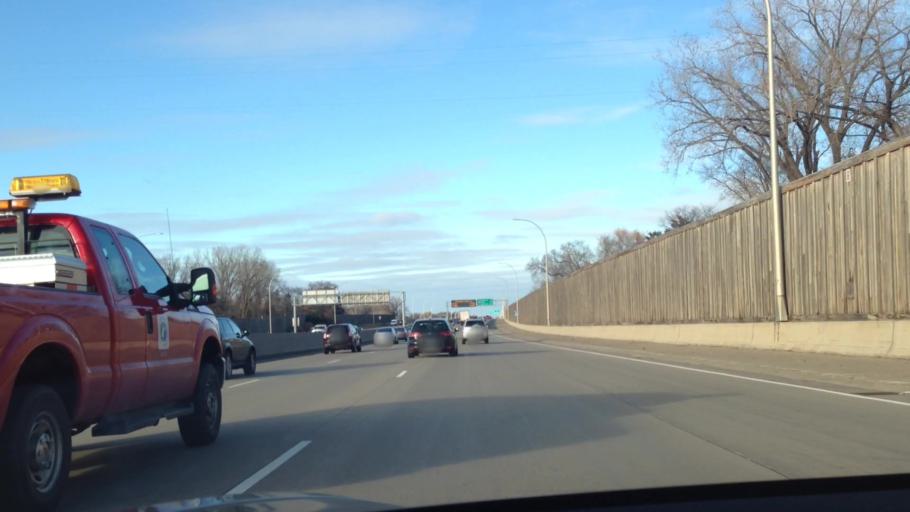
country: US
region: Minnesota
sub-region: Hennepin County
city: Golden Valley
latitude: 44.9892
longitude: -93.3492
